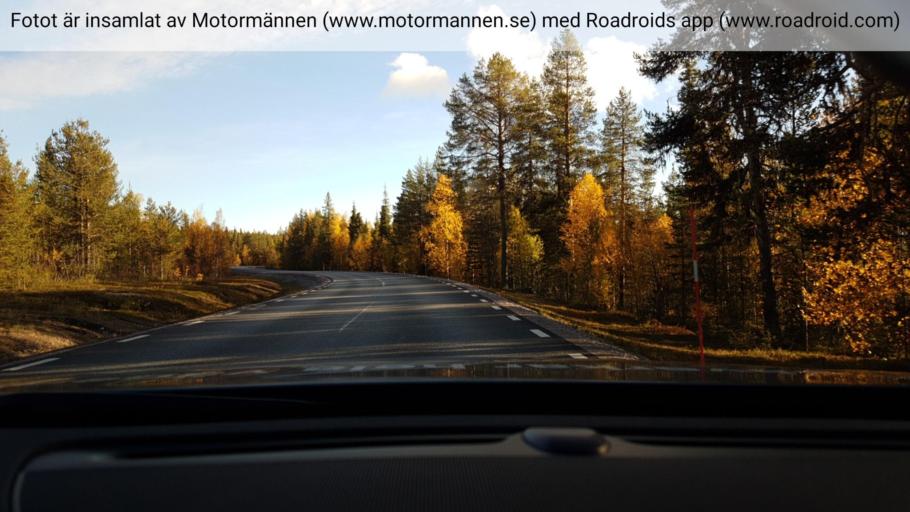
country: SE
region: Norrbotten
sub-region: Jokkmokks Kommun
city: Jokkmokk
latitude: 66.9204
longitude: 19.8286
